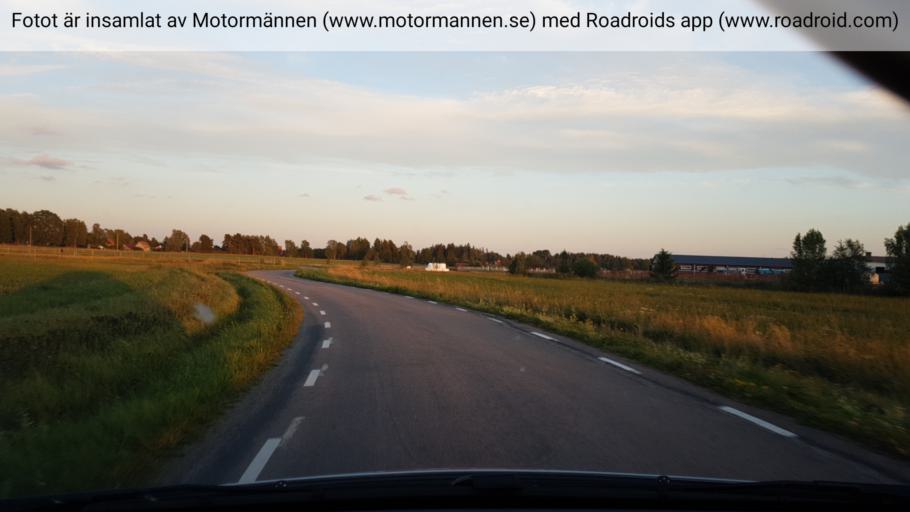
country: SE
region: Vaestmanland
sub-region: Hallstahammars Kommun
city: Kolback
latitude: 59.5615
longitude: 16.2034
